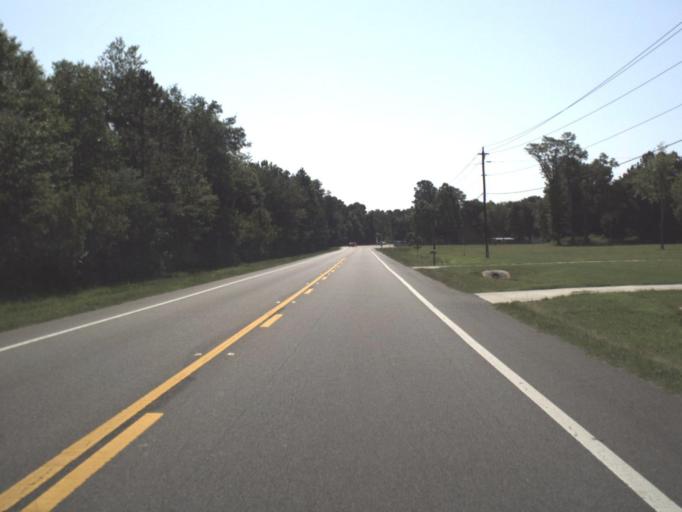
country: US
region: Florida
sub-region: Nassau County
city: Nassau Village-Ratliff
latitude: 30.5490
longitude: -81.7880
